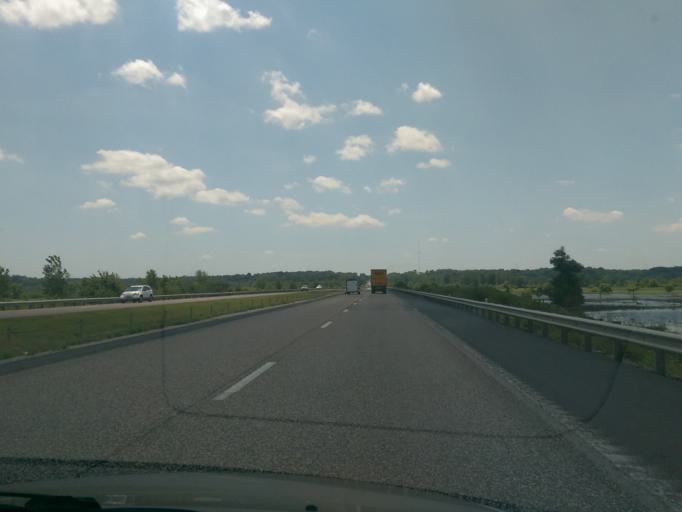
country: US
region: Missouri
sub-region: Cooper County
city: Boonville
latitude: 38.9535
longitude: -92.5550
